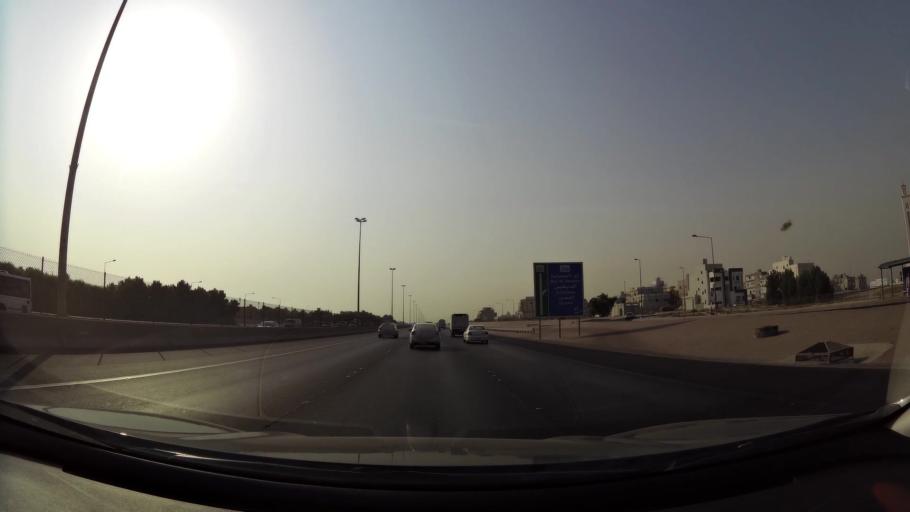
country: KW
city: Al Funaytis
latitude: 29.2339
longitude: 48.0965
